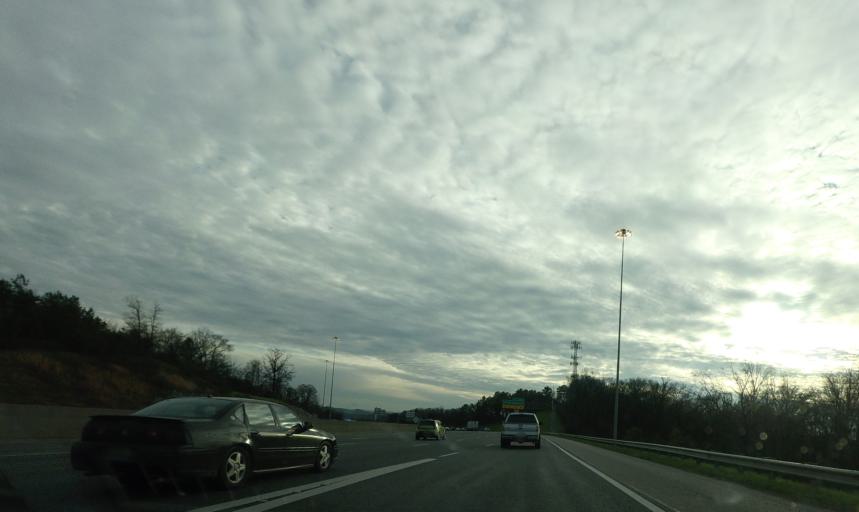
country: US
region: Alabama
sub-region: Jefferson County
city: Birmingham
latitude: 33.5583
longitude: -86.8308
